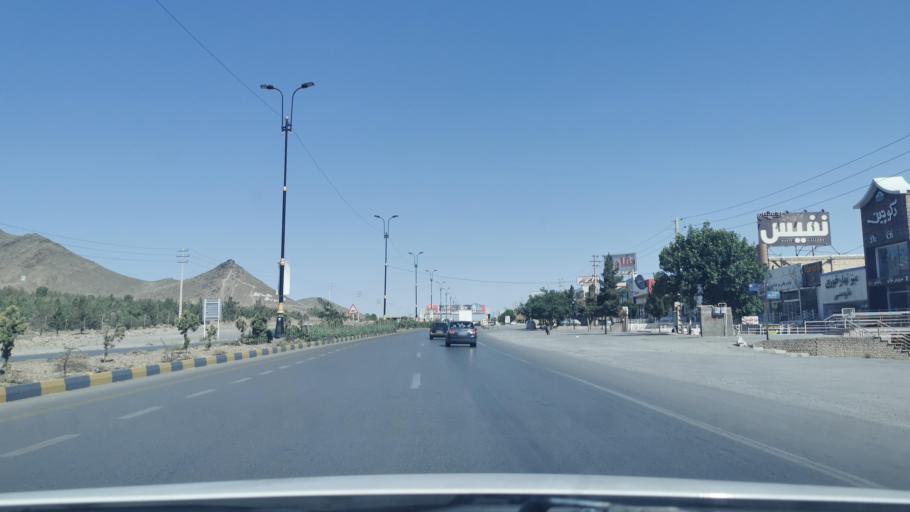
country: IR
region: Razavi Khorasan
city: Torqabeh
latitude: 36.3912
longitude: 59.4044
